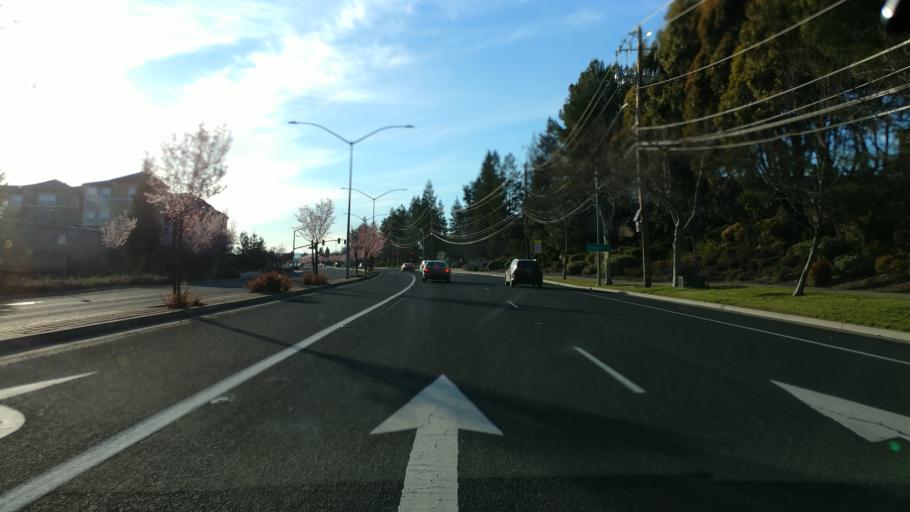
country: US
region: California
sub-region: Contra Costa County
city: Blackhawk
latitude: 37.7995
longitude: -121.8906
